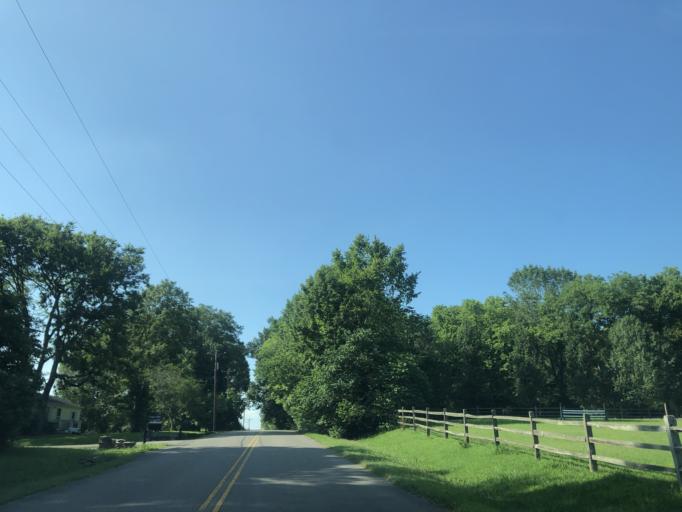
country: US
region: Tennessee
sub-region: Wilson County
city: Green Hill
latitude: 36.1419
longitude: -86.5950
